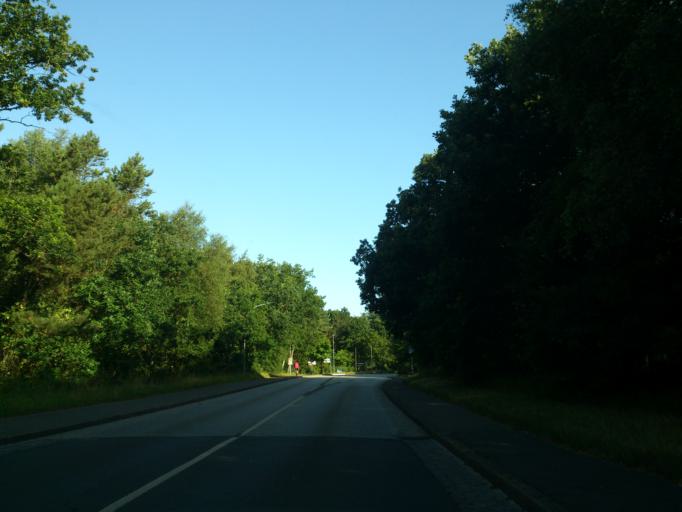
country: DE
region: Schleswig-Holstein
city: Sankt Peter-Ording
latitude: 54.3185
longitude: 8.6120
